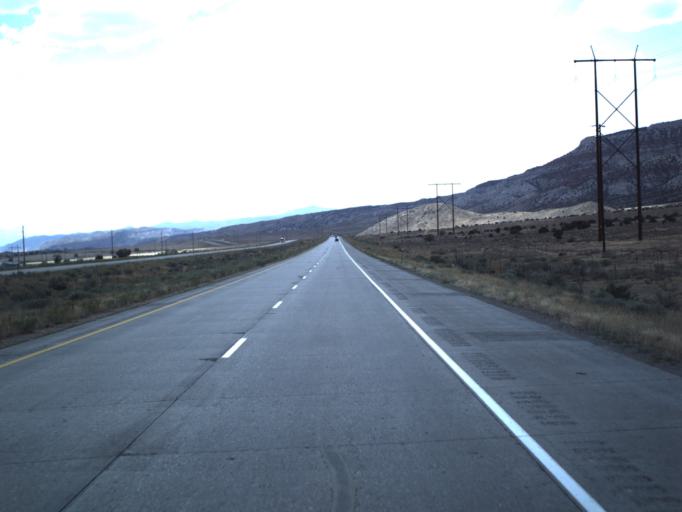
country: US
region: Utah
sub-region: Sevier County
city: Richfield
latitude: 38.8449
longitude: -112.0139
